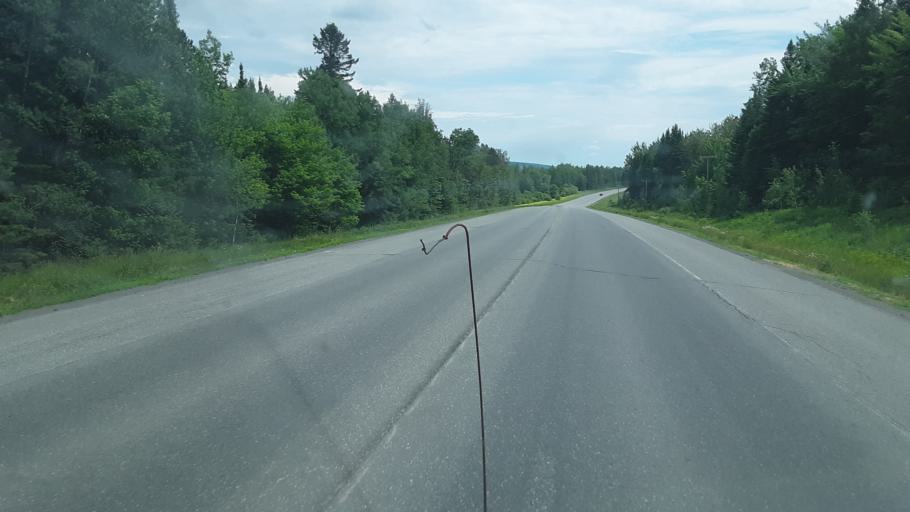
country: US
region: Maine
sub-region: Aroostook County
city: Caribou
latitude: 46.8371
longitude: -67.9999
